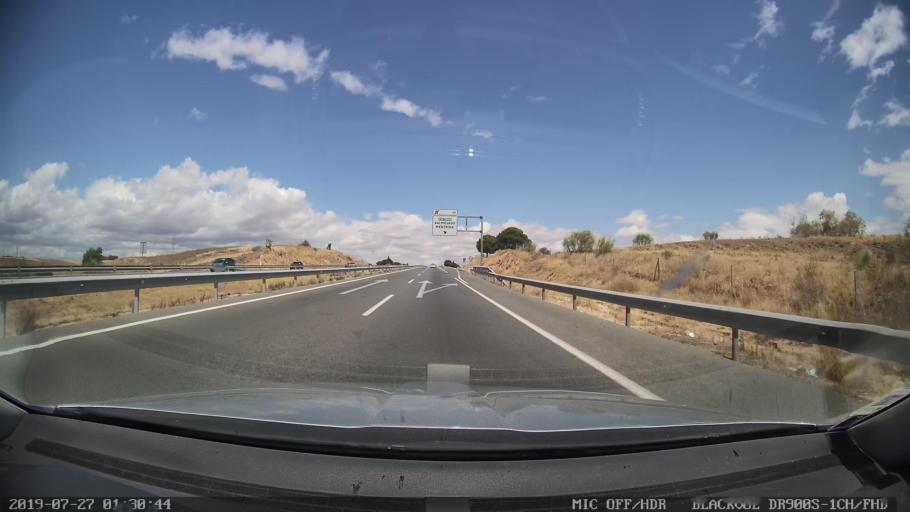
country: ES
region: Castille-La Mancha
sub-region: Province of Toledo
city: Valmojado
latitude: 40.2030
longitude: -4.1035
